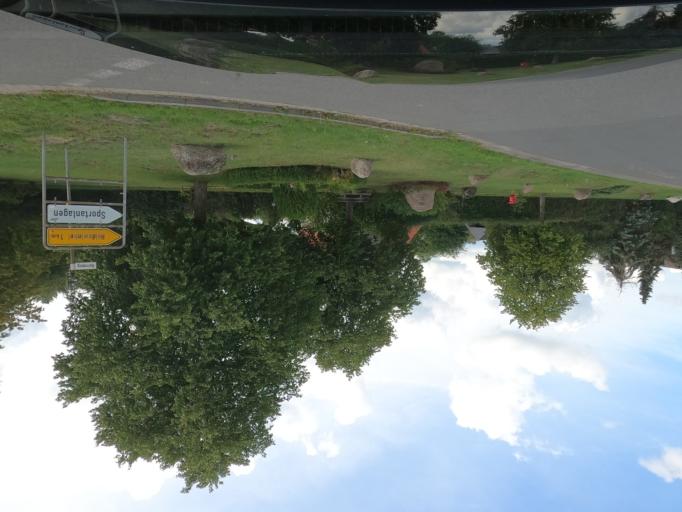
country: DE
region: Lower Saxony
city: Isernhagen Farster Bauerschaft
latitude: 52.5132
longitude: 9.8702
